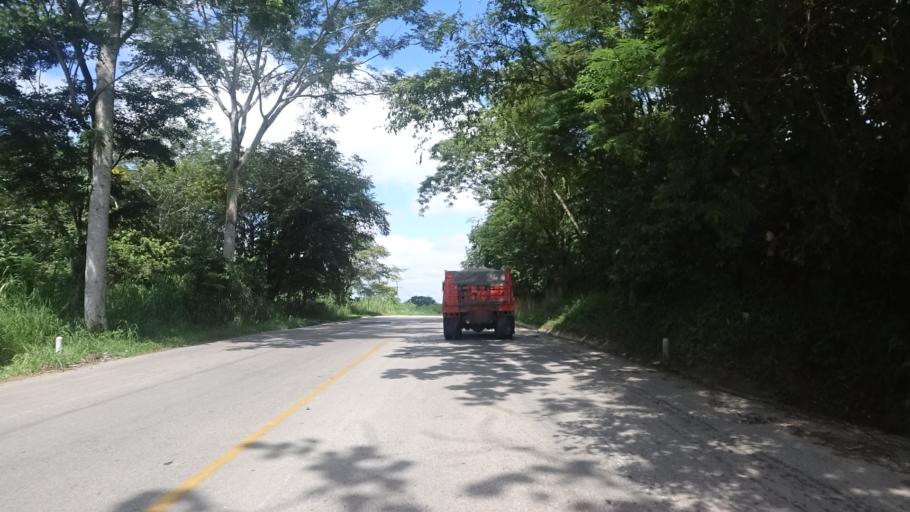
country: MX
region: Chiapas
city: Palenque
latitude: 17.4990
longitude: -91.9891
